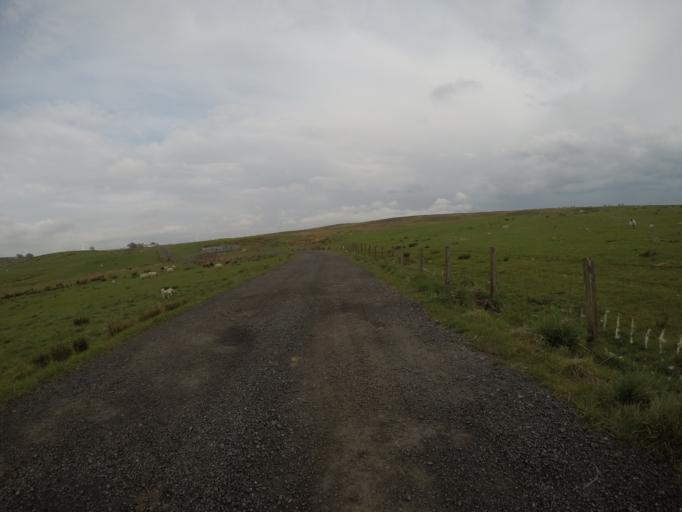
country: GB
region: Scotland
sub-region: East Ayrshire
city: Galston
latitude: 55.6852
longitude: -4.4048
